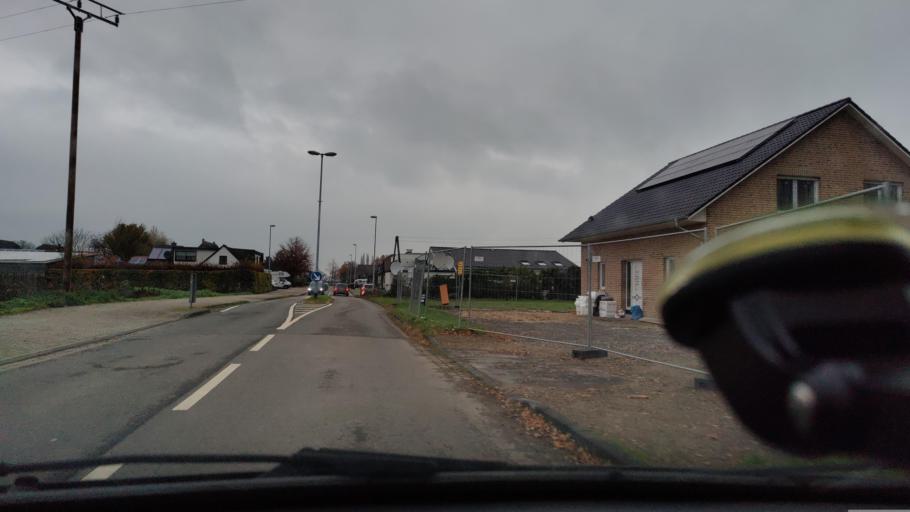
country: DE
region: North Rhine-Westphalia
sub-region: Regierungsbezirk Dusseldorf
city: Kamp-Lintfort
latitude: 51.5326
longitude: 6.5483
